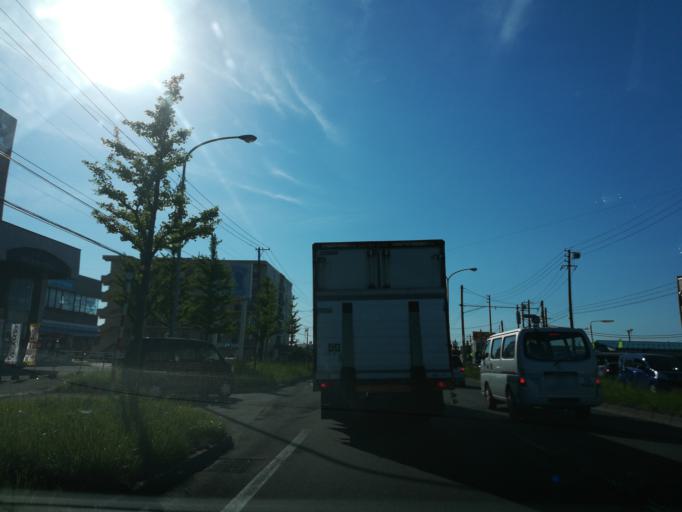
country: JP
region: Hokkaido
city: Kitahiroshima
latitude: 43.0234
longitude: 141.4689
